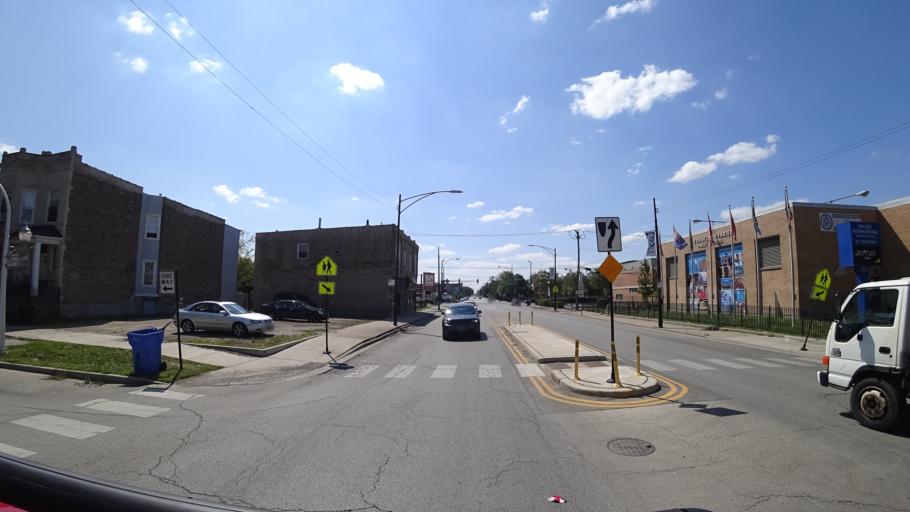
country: US
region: Illinois
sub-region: Cook County
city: Cicero
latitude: 41.8671
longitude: -87.7252
